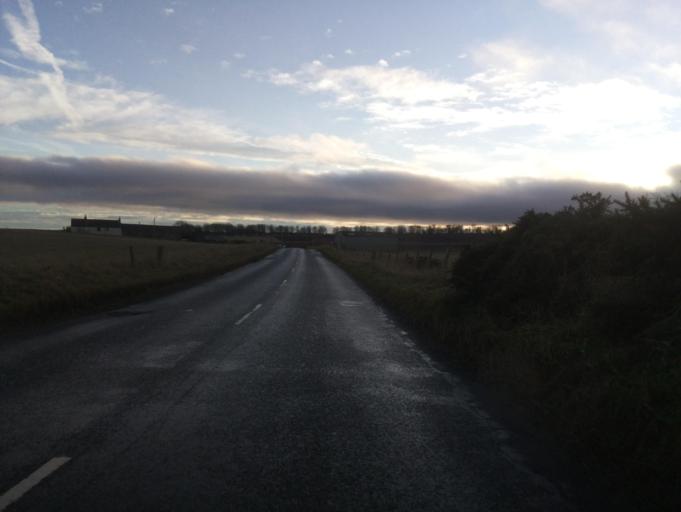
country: GB
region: Scotland
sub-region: Angus
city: Letham
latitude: 56.5738
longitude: -2.7802
